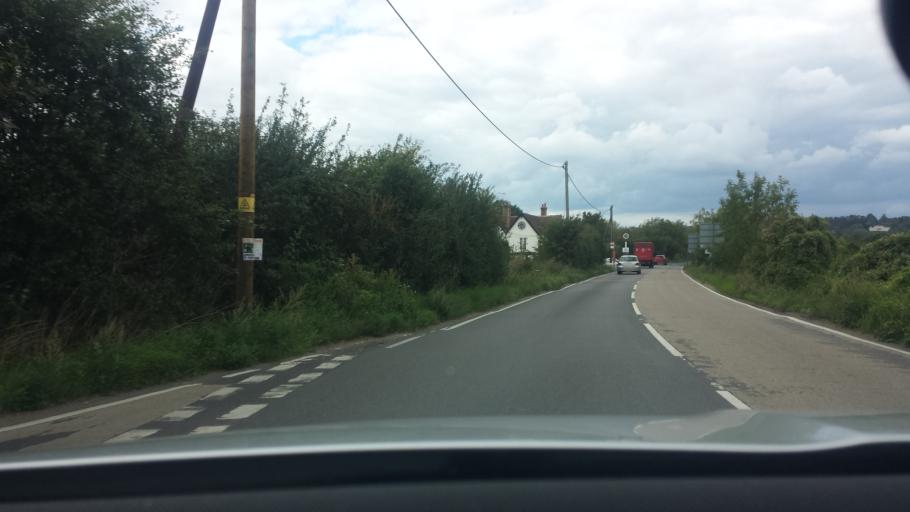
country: GB
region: England
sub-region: Kent
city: Marden
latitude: 51.2005
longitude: 0.5174
